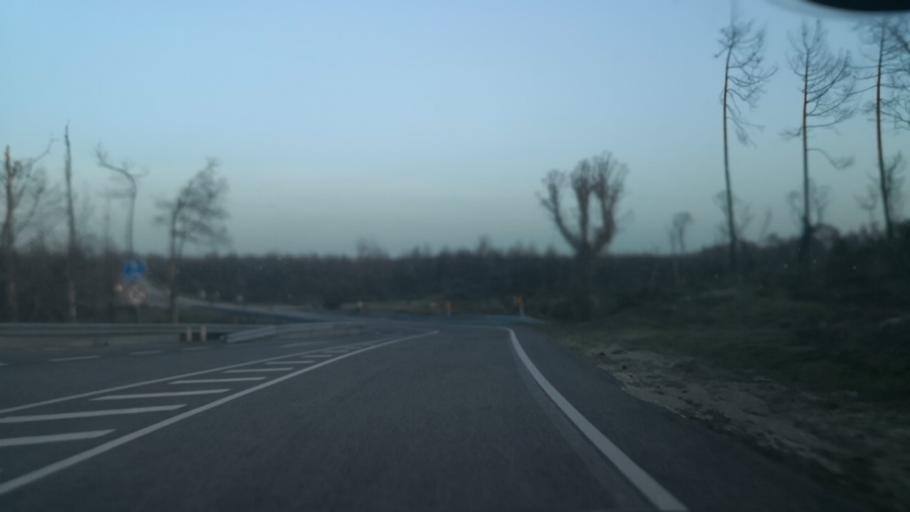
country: PT
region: Leiria
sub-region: Marinha Grande
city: Marinha Grande
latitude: 39.7472
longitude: -8.9759
